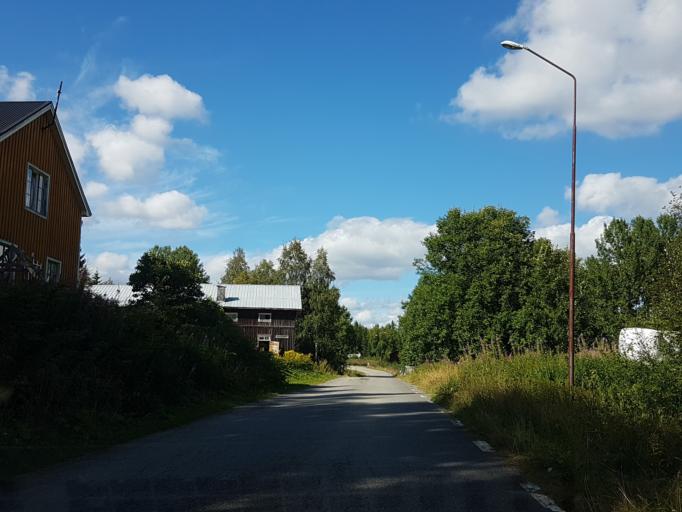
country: SE
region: Vaesterbotten
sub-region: Skelleftea Kommun
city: Burtraesk
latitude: 64.2697
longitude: 20.4913
